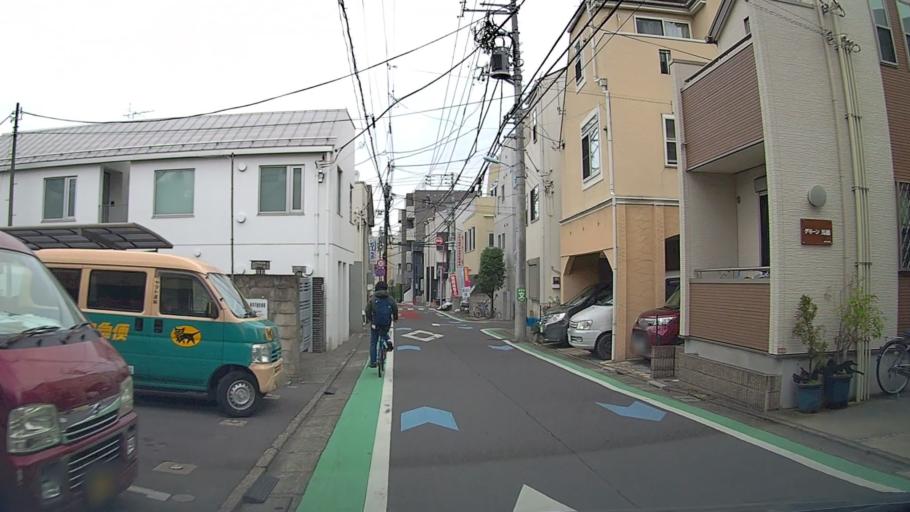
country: JP
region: Tokyo
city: Tokyo
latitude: 35.7022
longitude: 139.6438
